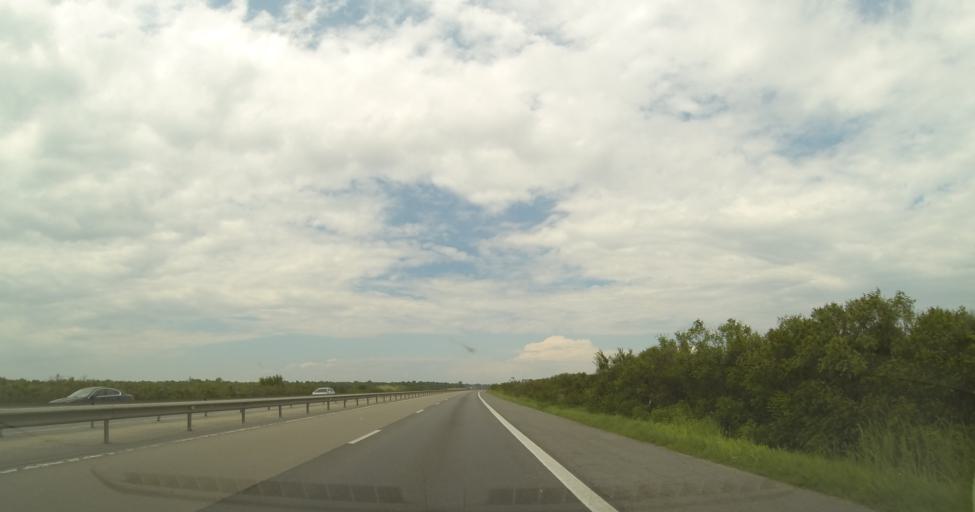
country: RO
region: Dambovita
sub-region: Comuna Corbii Mari
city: Grozavesti
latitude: 44.5918
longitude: 25.4621
